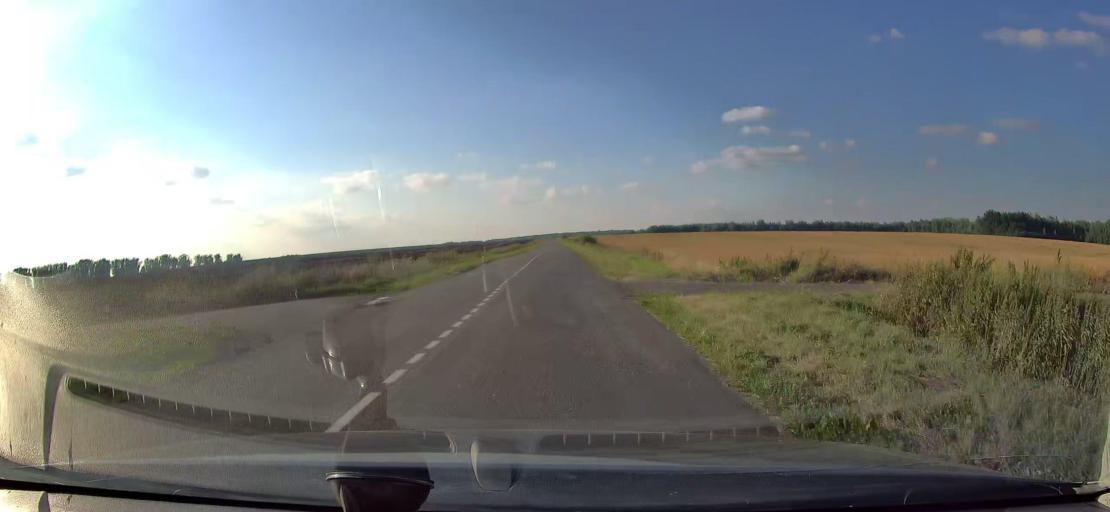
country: RU
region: Kursk
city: Zolotukhino
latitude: 52.0480
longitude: 36.2068
